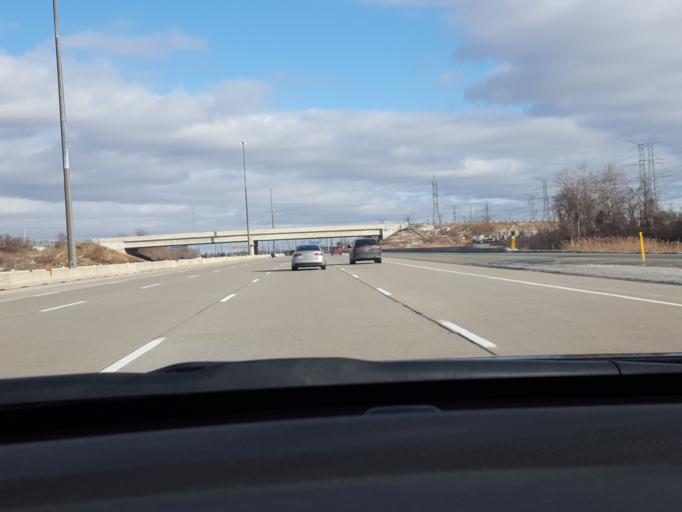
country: CA
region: Ontario
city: Markham
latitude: 43.8418
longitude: -79.3493
